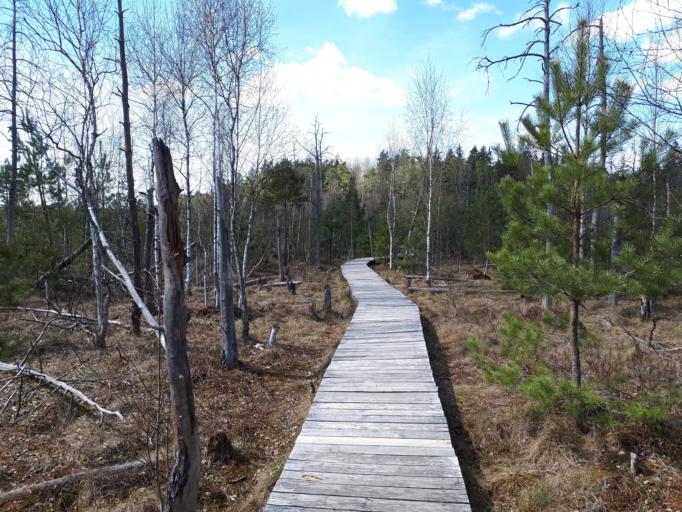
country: LT
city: Ramuciai
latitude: 54.8486
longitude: 24.0749
